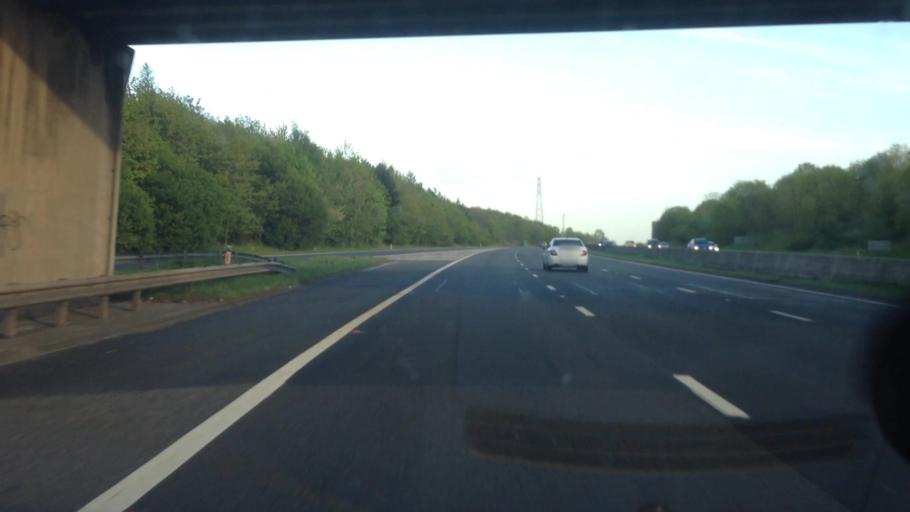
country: GB
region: England
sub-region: Barnsley
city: Birdwell
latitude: 53.4950
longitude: -1.4734
